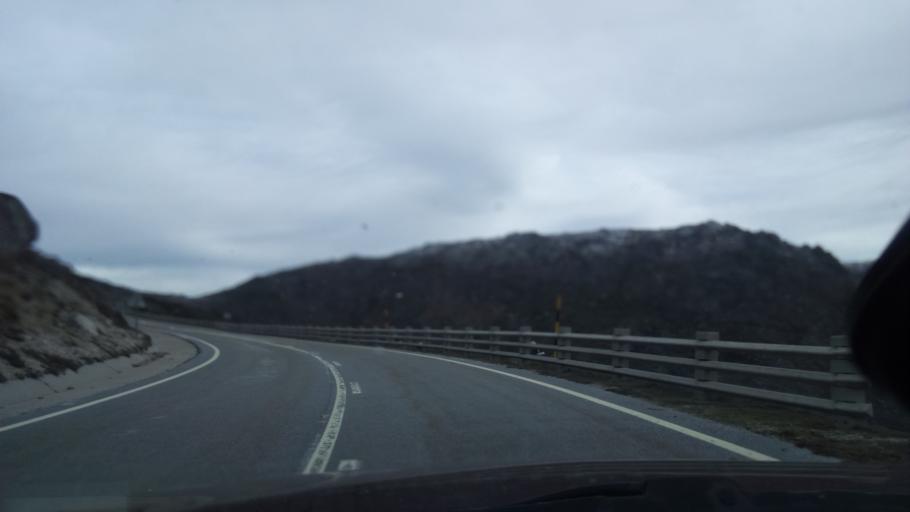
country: PT
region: Guarda
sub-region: Seia
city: Seia
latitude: 40.3443
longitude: -7.6948
